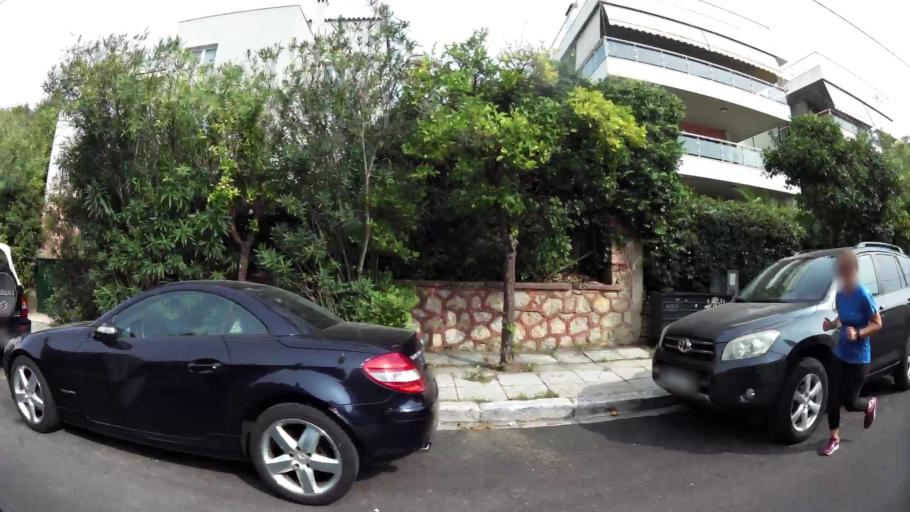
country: GR
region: Attica
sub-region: Nomarchia Athinas
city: Filothei
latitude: 38.0232
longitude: 23.7824
